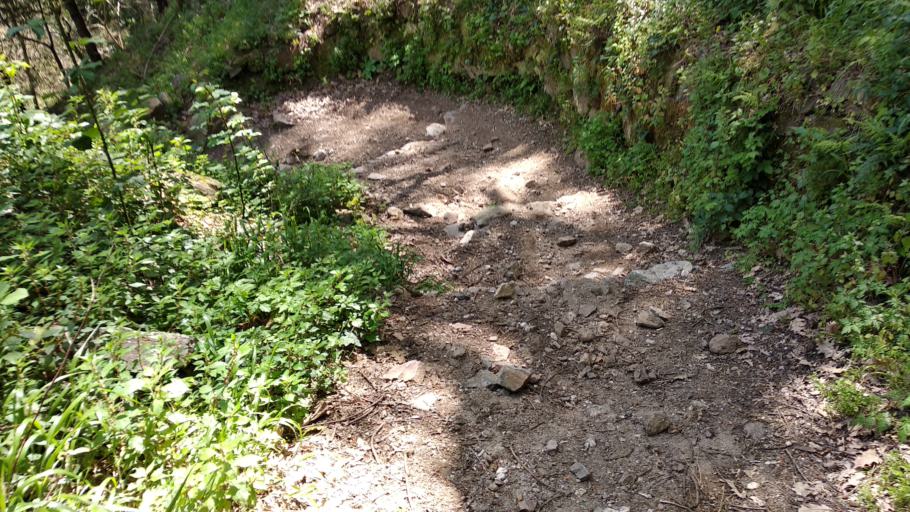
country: IT
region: Sicily
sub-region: Messina
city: Messina
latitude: 38.2141
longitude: 15.5075
